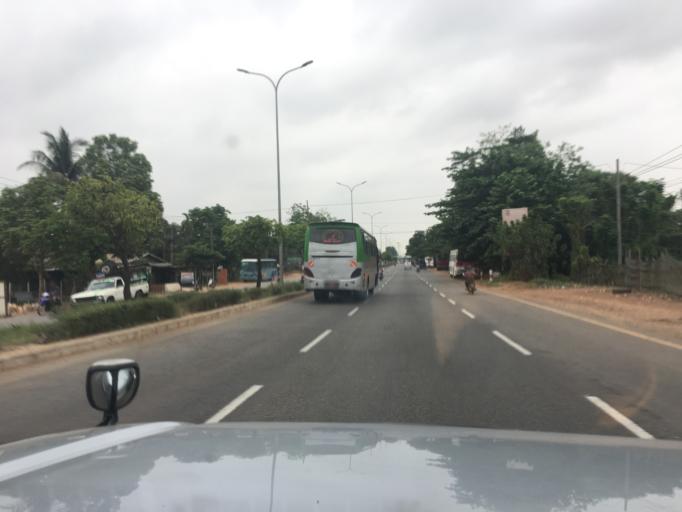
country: MM
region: Bago
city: Bago
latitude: 17.2491
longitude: 96.4669
